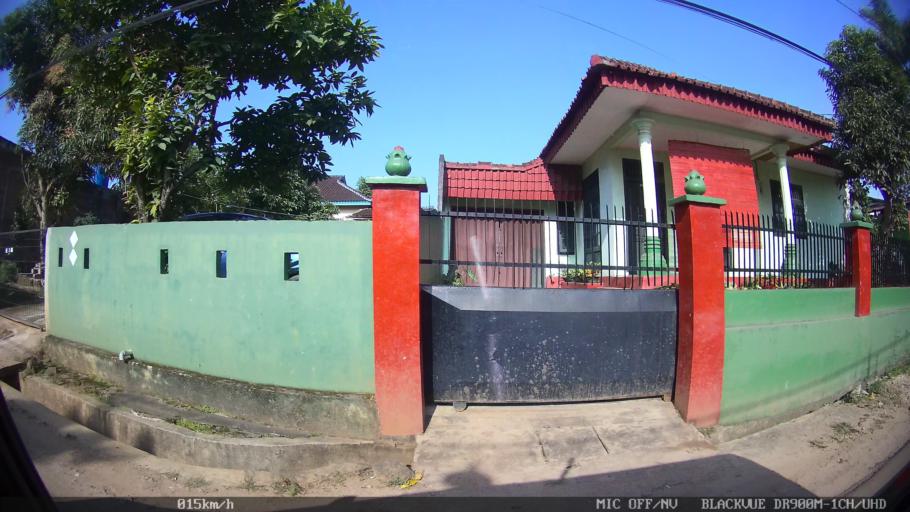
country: ID
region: Lampung
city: Kedaton
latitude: -5.3719
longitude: 105.2333
